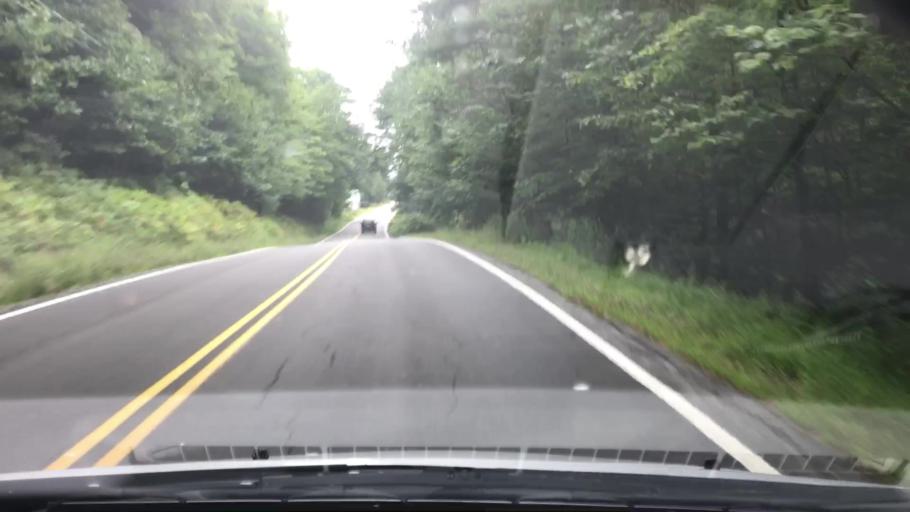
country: US
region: New Hampshire
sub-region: Grafton County
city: Woodsville
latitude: 44.1827
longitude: -72.0509
